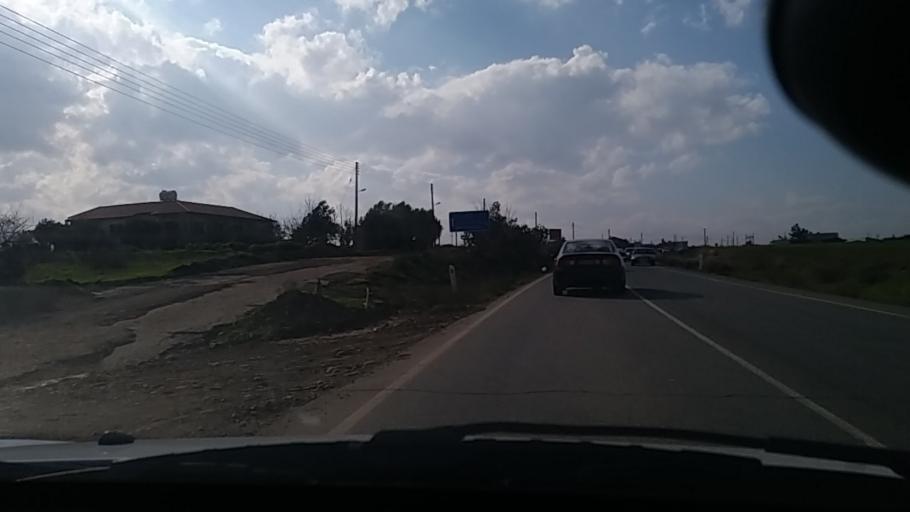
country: CY
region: Lefkosia
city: Akaki
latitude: 35.1378
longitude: 33.1538
